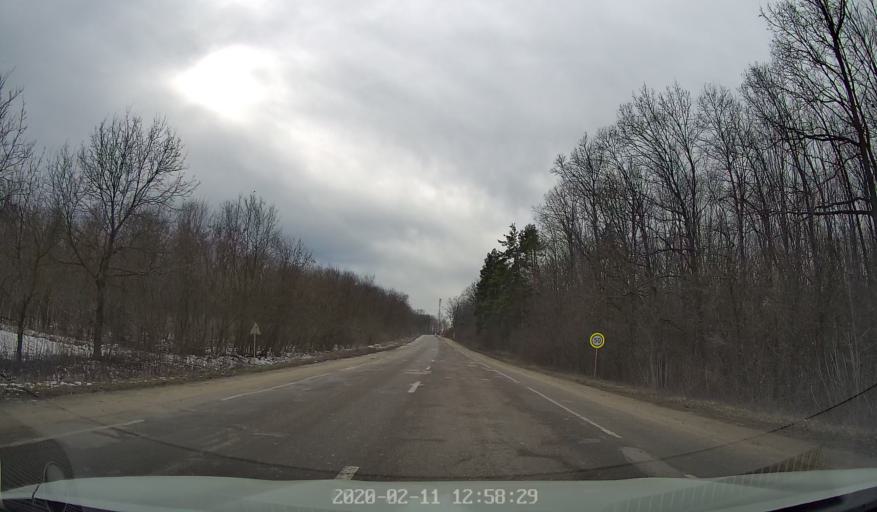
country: MD
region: Briceni
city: Briceni
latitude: 48.3345
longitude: 27.0518
